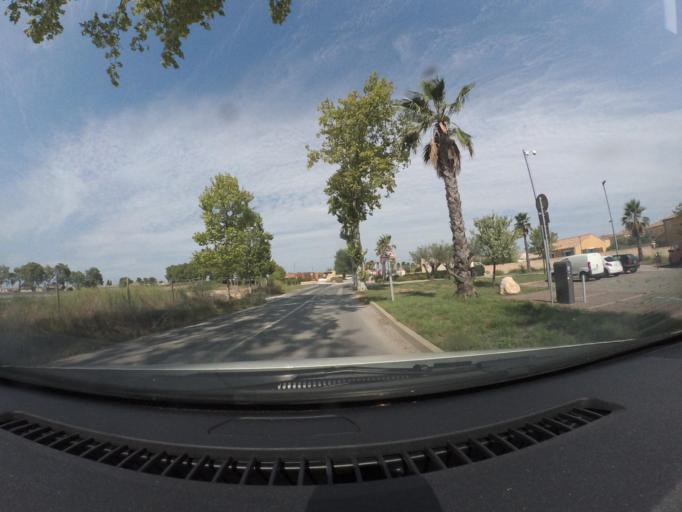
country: FR
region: Languedoc-Roussillon
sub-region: Departement de l'Herault
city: Baillargues
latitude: 43.6548
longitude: 4.0083
